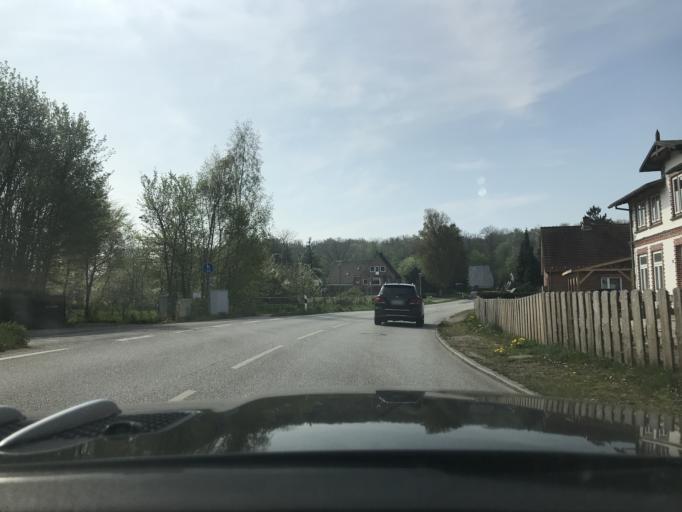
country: DE
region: Schleswig-Holstein
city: Gromitz
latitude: 54.1815
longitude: 10.9820
